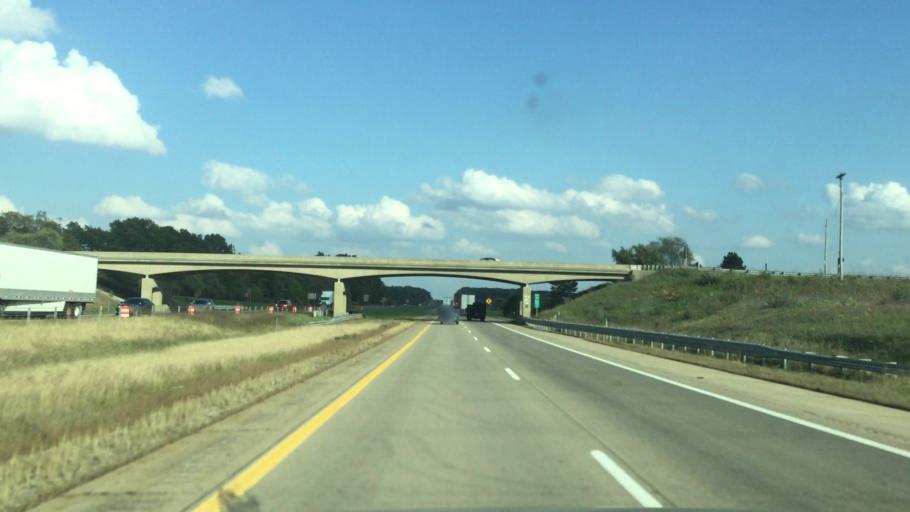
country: US
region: Michigan
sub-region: Calhoun County
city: Marshall
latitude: 42.2830
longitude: -84.8639
